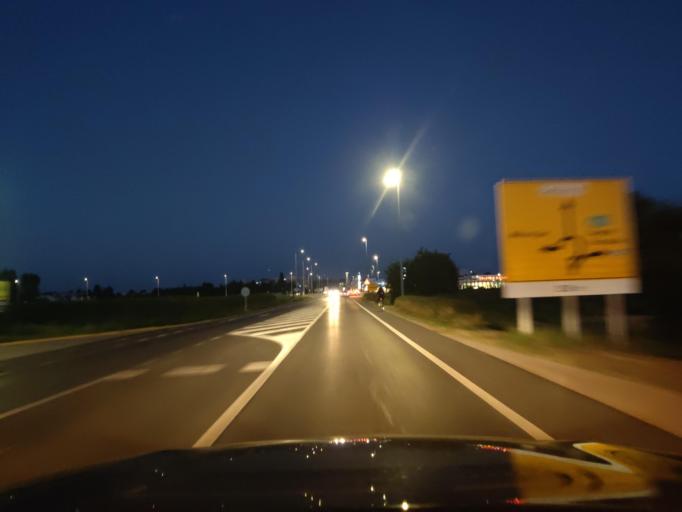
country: HR
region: Medimurska
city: Senkovec
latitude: 46.3992
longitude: 16.4264
